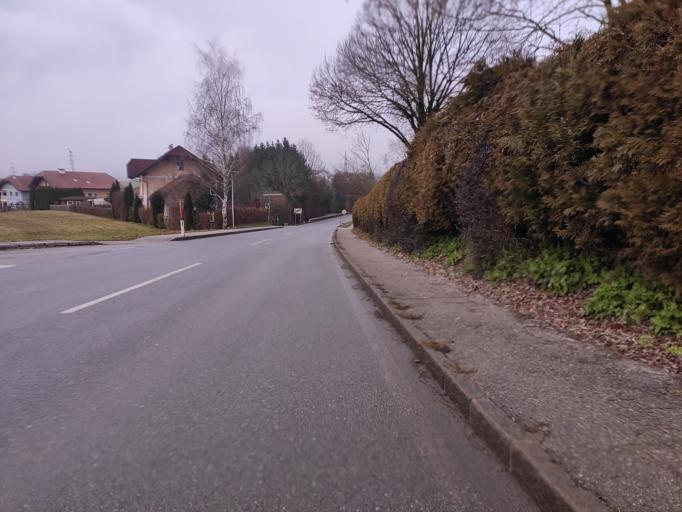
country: AT
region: Salzburg
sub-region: Politischer Bezirk Salzburg-Umgebung
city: Kostendorf
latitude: 47.9537
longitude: 13.2078
